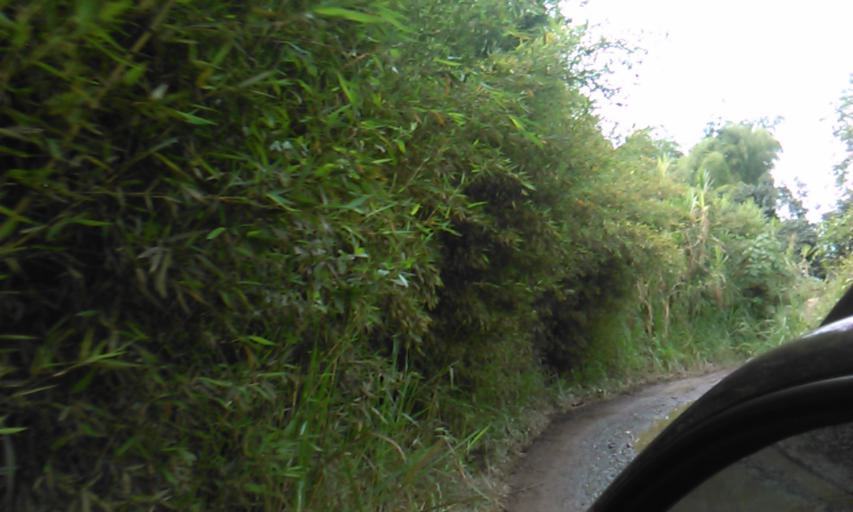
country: CO
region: Quindio
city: Cordoba
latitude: 4.4043
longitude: -75.6884
